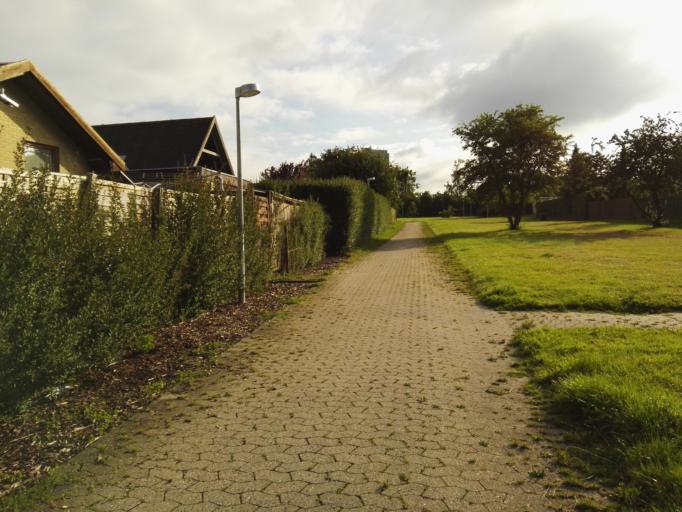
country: DK
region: Capital Region
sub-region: Ballerup Kommune
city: Ballerup
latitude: 55.7160
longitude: 12.3537
